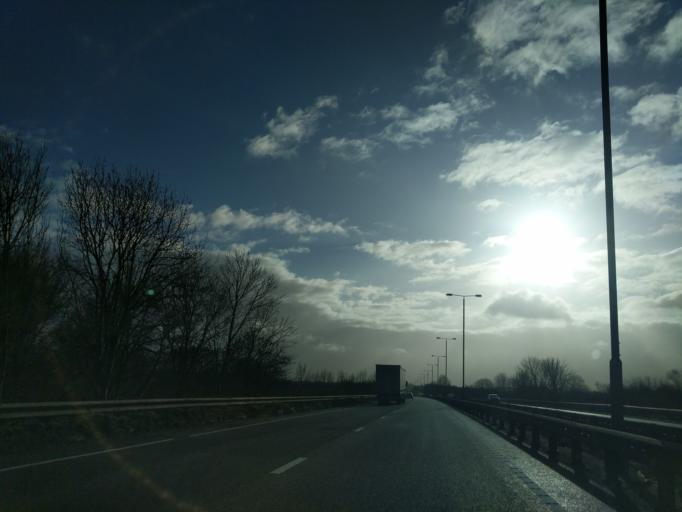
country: GB
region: England
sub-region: Derbyshire
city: Findern
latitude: 52.8958
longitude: -1.5399
